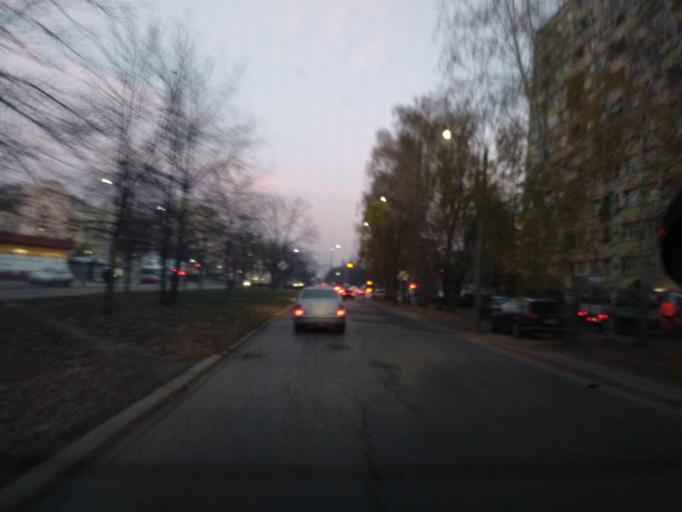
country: PL
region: Lower Silesian Voivodeship
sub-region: Powiat wroclawski
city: Wroclaw
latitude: 51.0961
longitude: 17.0150
